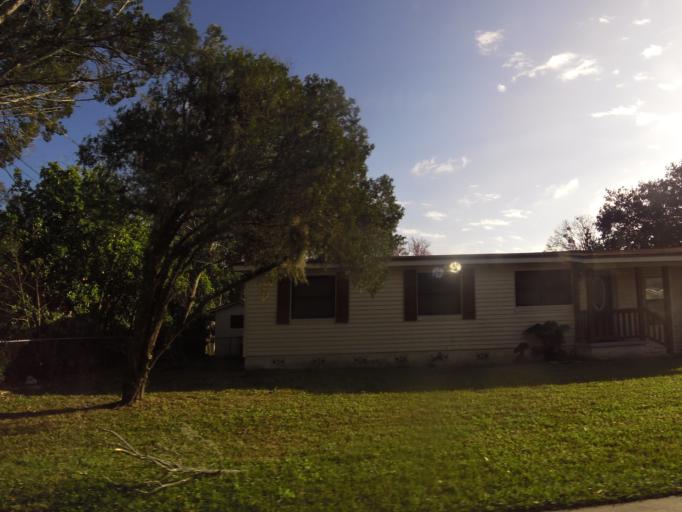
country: US
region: Florida
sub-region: Duval County
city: Jacksonville
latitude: 30.2772
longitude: -81.5943
